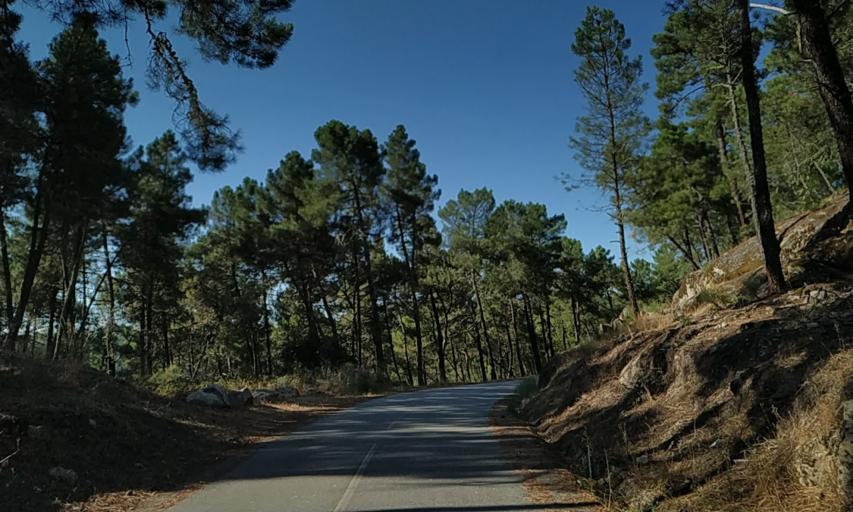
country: PT
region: Viseu
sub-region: Sao Joao da Pesqueira
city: Sao Joao da Pesqueira
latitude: 41.2514
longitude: -7.4272
